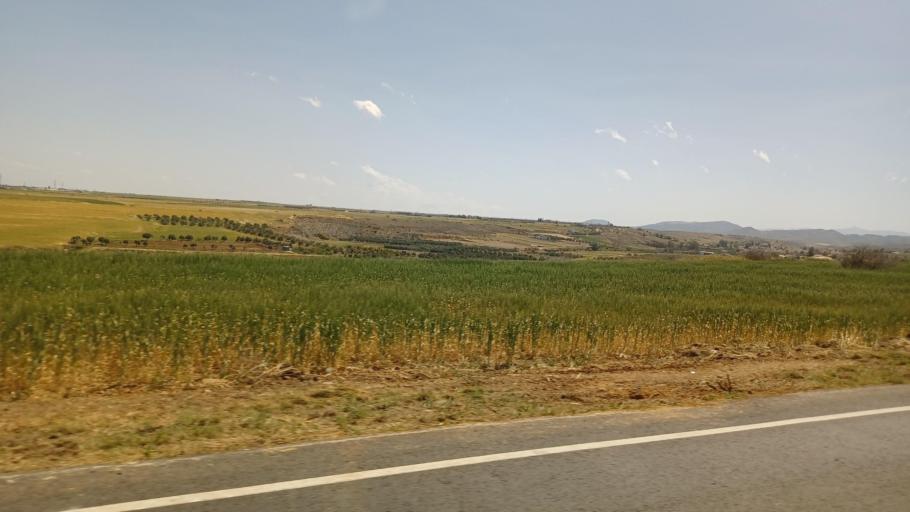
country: CY
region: Lefkosia
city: Astromeritis
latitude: 35.1185
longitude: 33.0146
